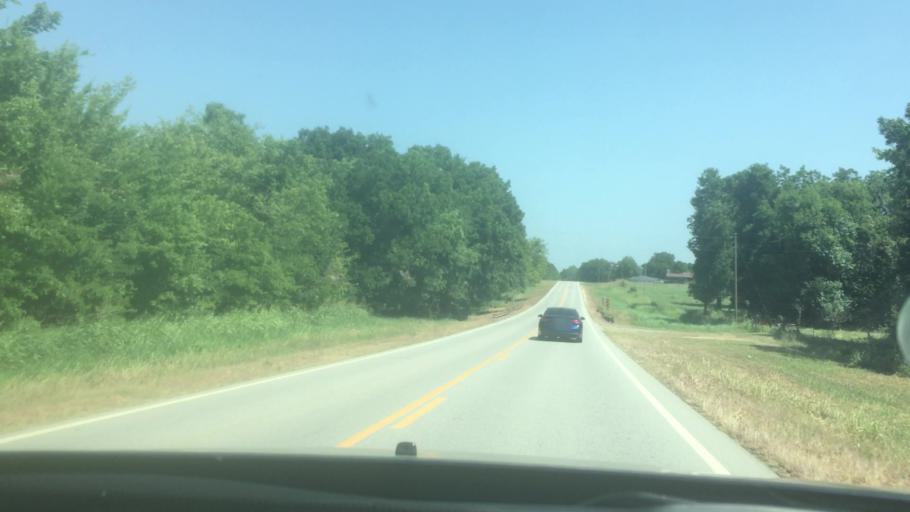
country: US
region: Oklahoma
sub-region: Coal County
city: Coalgate
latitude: 34.5266
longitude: -96.4070
